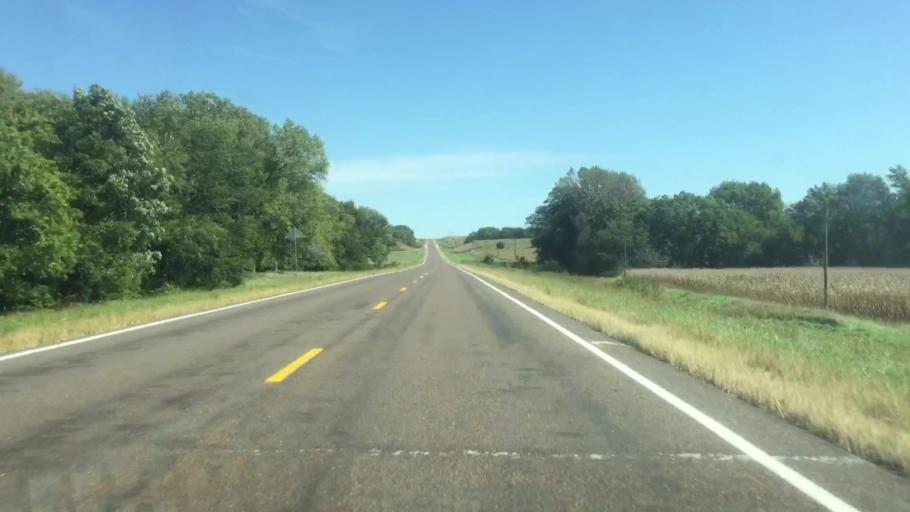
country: US
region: Nebraska
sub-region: Gage County
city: Wymore
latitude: 40.0452
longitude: -96.7833
